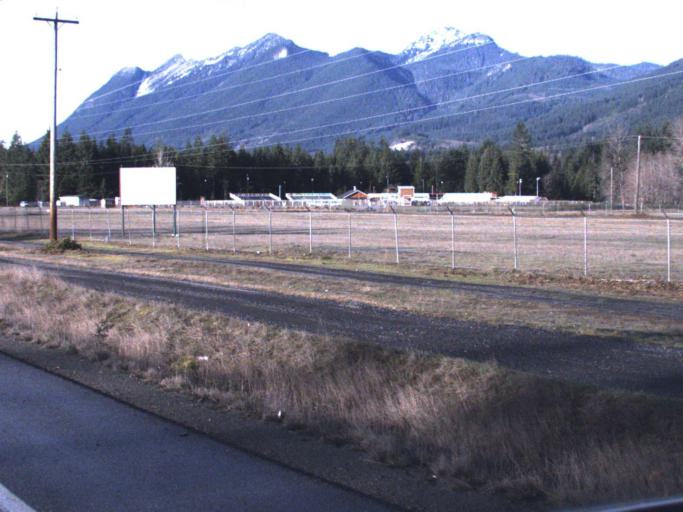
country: US
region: Washington
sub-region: Snohomish County
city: Darrington
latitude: 48.2730
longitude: -121.6572
